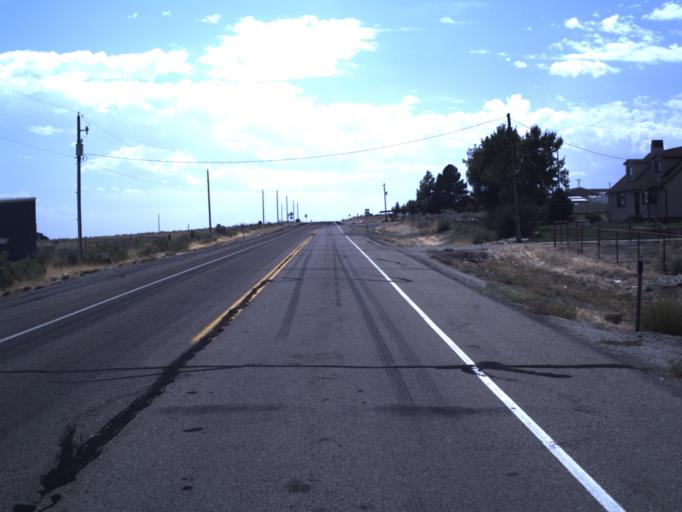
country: US
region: Utah
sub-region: Utah County
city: Eagle Mountain
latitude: 40.3247
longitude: -112.1024
